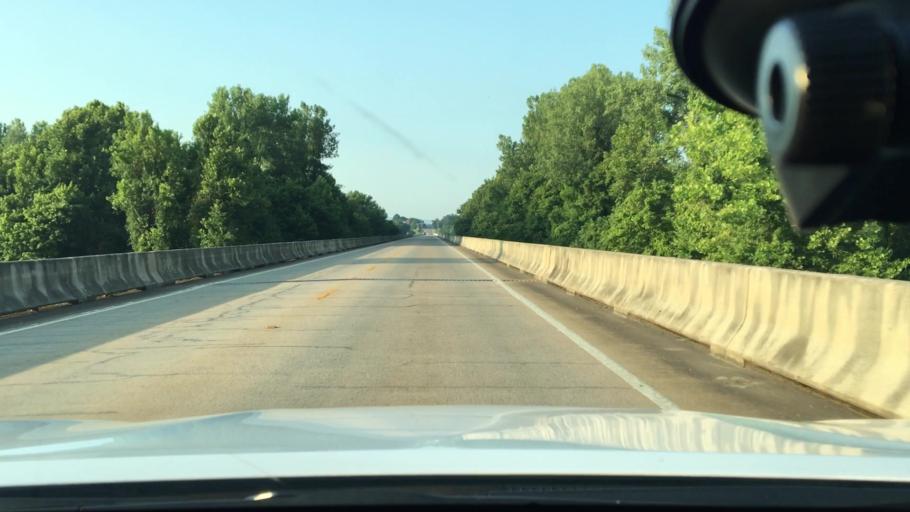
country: US
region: Arkansas
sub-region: Johnson County
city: Clarksville
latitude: 35.3993
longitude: -93.5310
